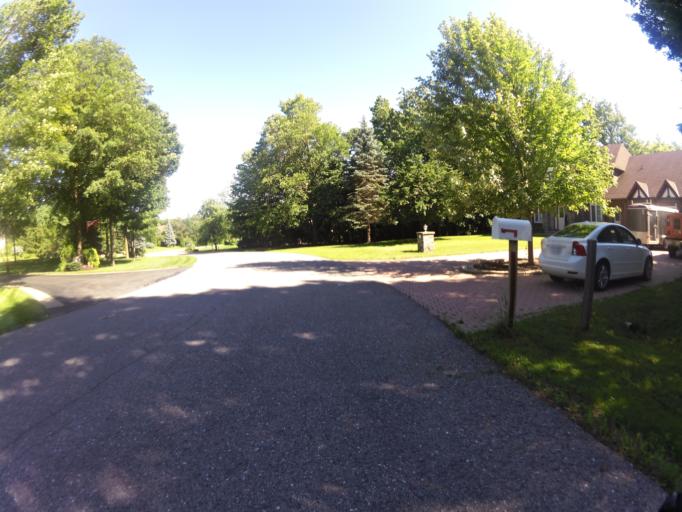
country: CA
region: Ontario
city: Bells Corners
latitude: 45.2840
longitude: -75.7892
